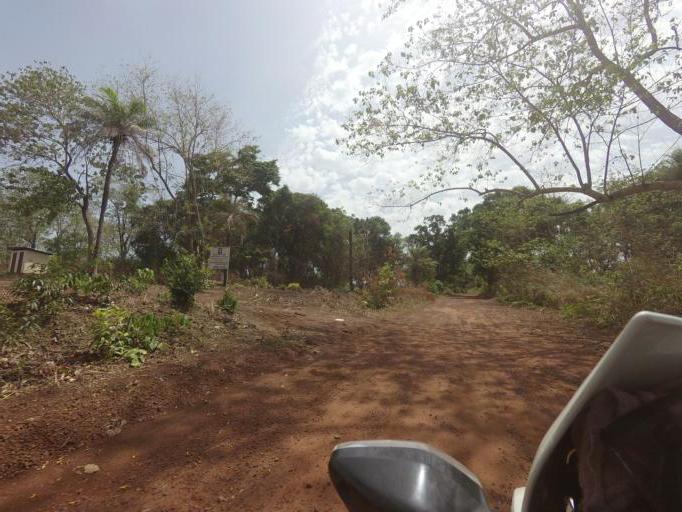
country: SL
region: Northern Province
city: Kamakwie
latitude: 9.4823
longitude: -12.2407
